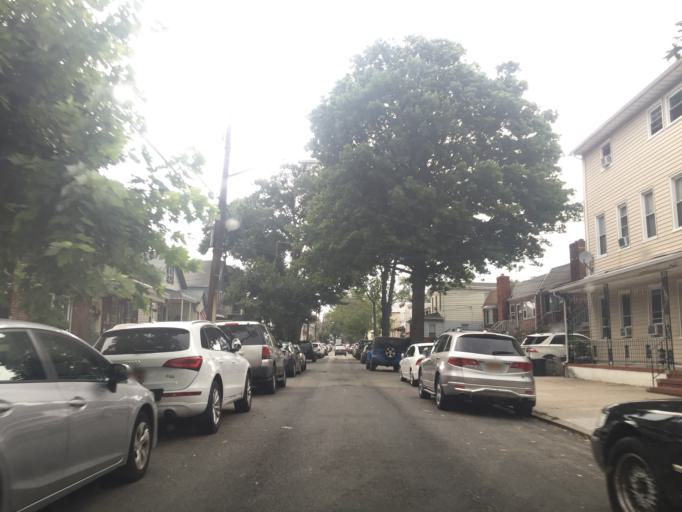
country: US
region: New York
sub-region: Bronx
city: The Bronx
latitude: 40.7819
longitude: -73.8477
